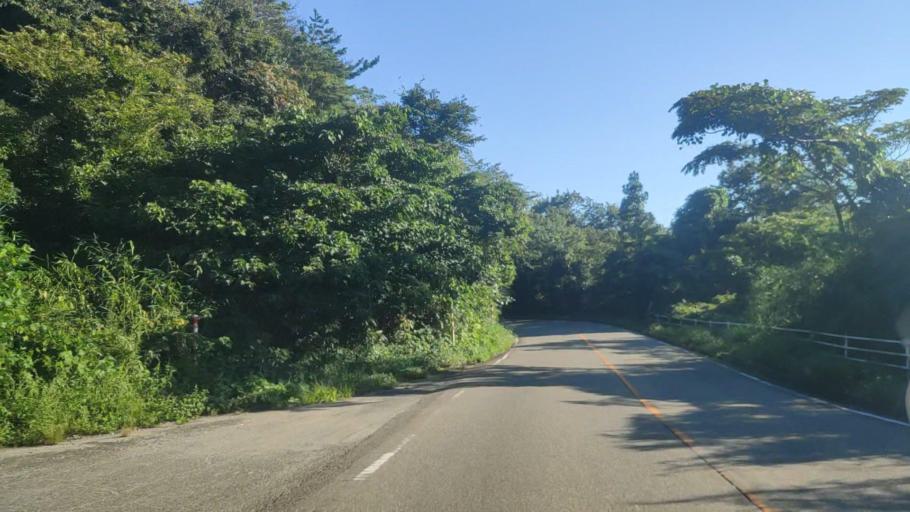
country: JP
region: Ishikawa
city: Nanao
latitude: 37.1000
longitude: 136.9499
